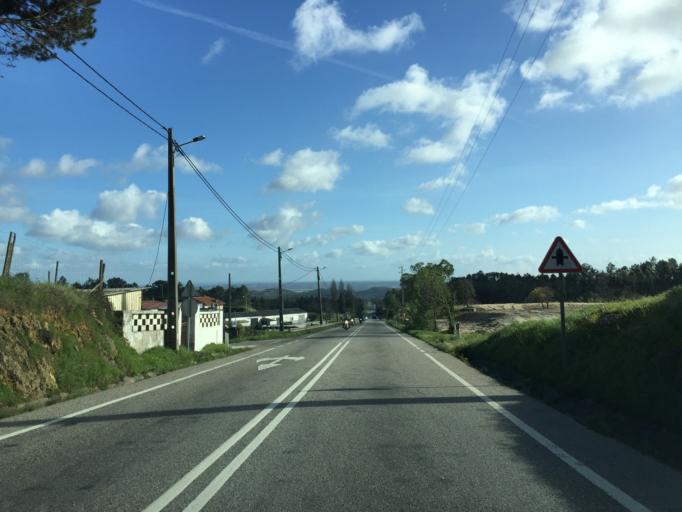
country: PT
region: Coimbra
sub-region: Figueira da Foz
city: Tavarede
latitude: 40.1886
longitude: -8.8300
